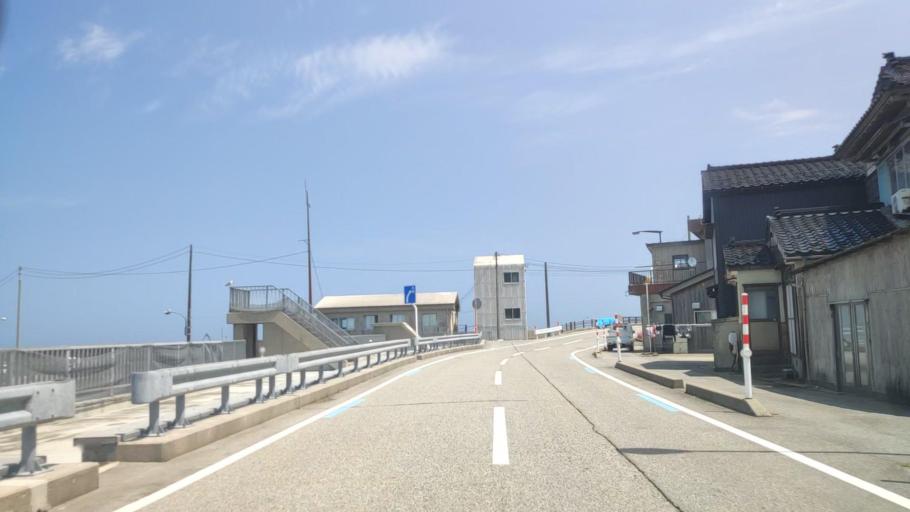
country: JP
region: Toyama
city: Nyuzen
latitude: 36.9730
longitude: 137.5868
